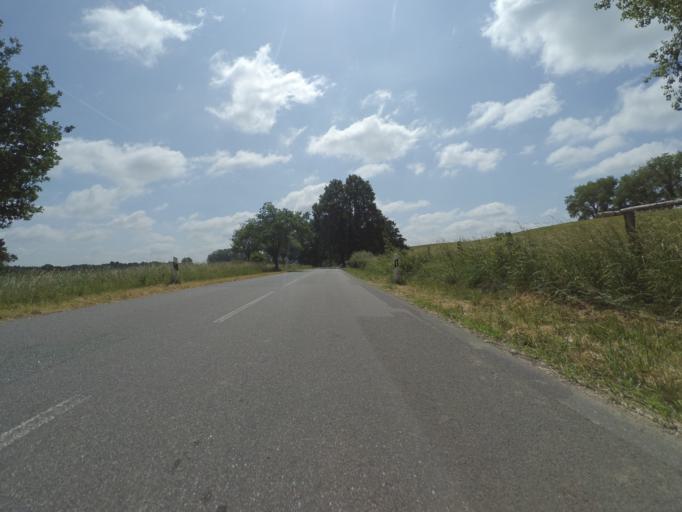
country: DE
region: Mecklenburg-Vorpommern
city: Neuburg
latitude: 53.4611
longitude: 11.9423
